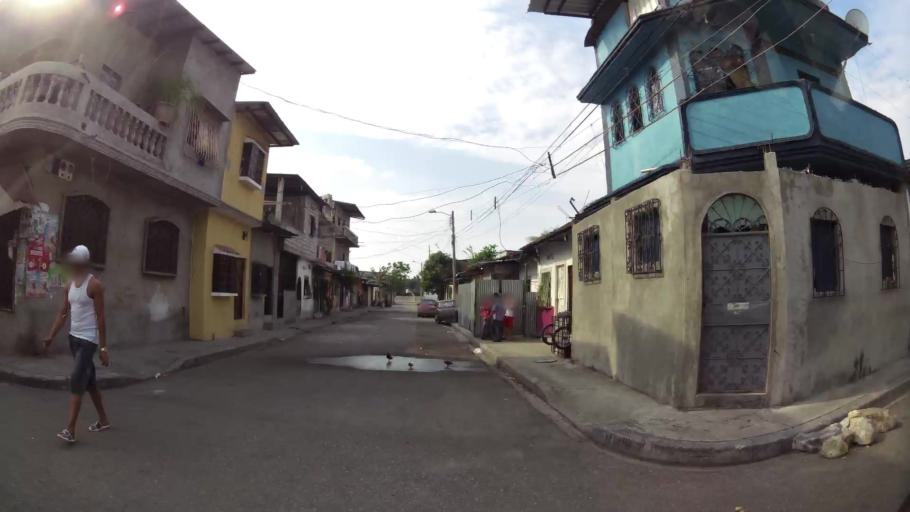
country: EC
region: Guayas
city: Guayaquil
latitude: -2.2483
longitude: -79.9104
